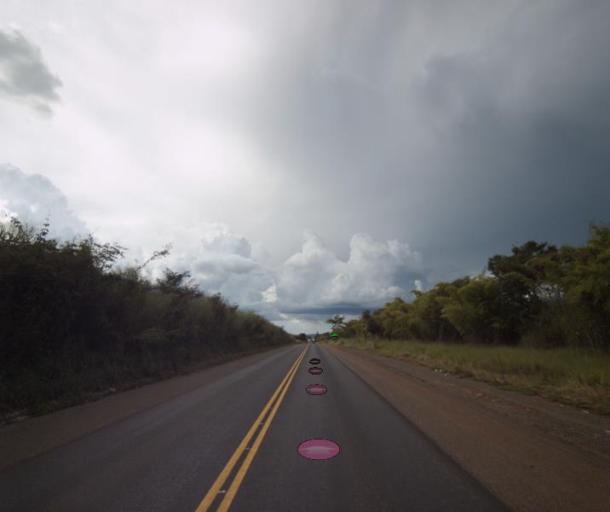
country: BR
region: Goias
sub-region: Ceres
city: Ceres
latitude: -15.2022
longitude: -49.5449
